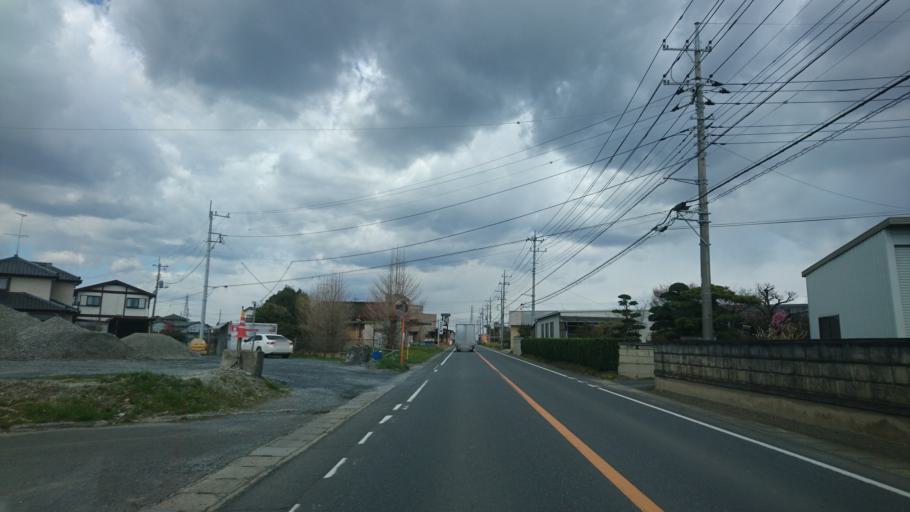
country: JP
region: Ibaraki
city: Yuki
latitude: 36.2381
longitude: 139.9323
